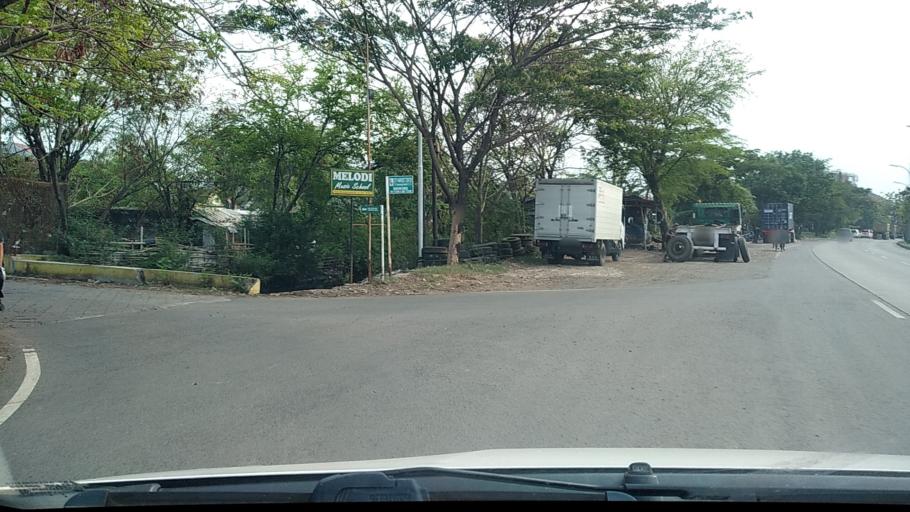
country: ID
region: Central Java
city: Semarang
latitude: -6.9678
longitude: 110.3932
